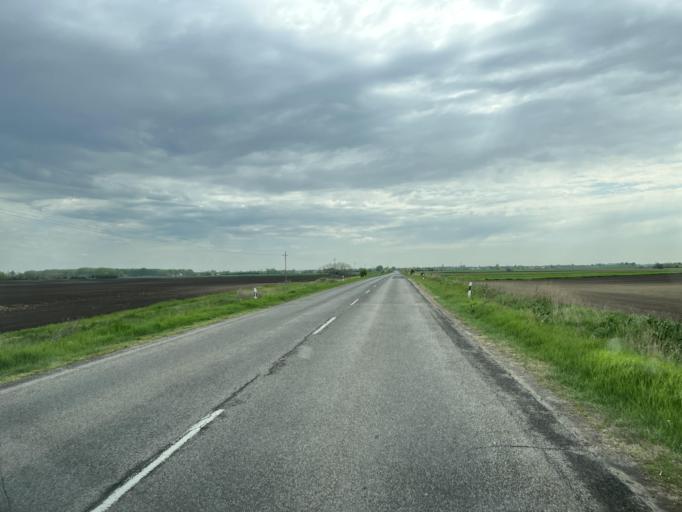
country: HU
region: Pest
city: Abony
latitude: 47.1892
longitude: 19.9616
